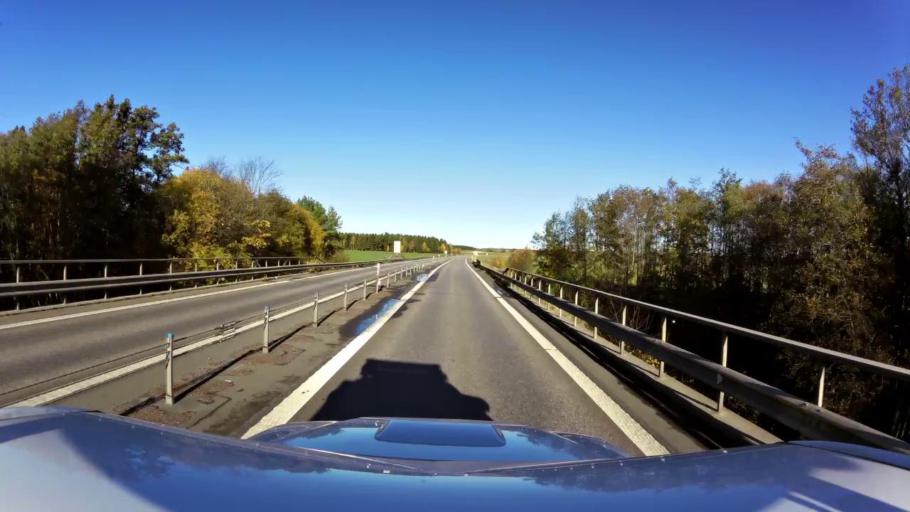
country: SE
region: OEstergoetland
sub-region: Linkopings Kommun
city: Berg
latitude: 58.4532
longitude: 15.5040
